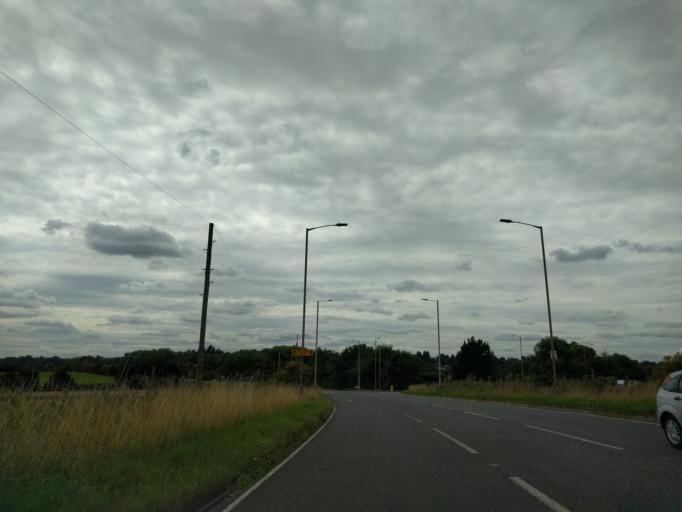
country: GB
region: England
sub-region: Essex
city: Great Dunmow
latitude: 51.8729
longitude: 0.3776
